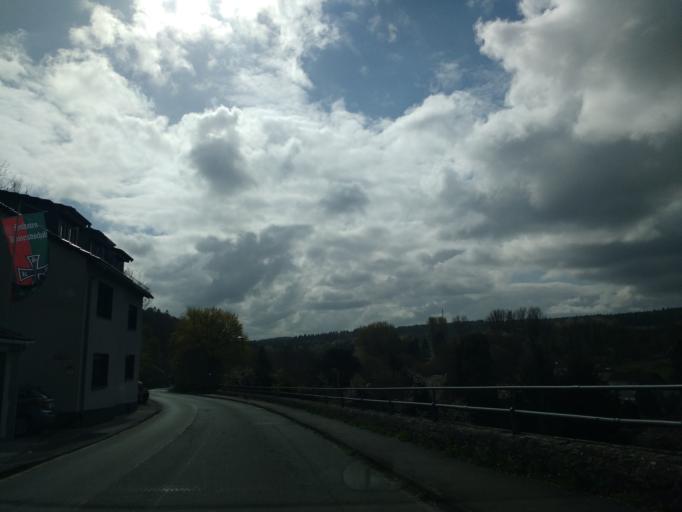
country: DE
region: North Rhine-Westphalia
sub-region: Regierungsbezirk Detmold
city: Wunnenberg
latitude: 51.5121
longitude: 8.7418
